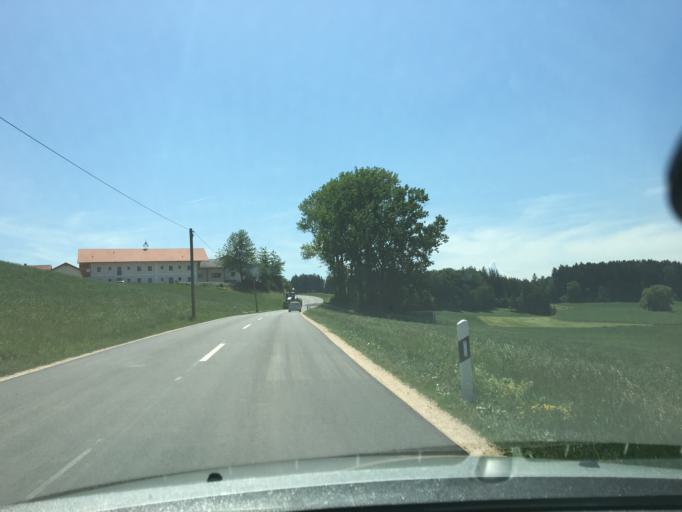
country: DE
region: Bavaria
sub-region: Upper Bavaria
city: Halsbach
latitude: 48.1203
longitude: 12.6792
